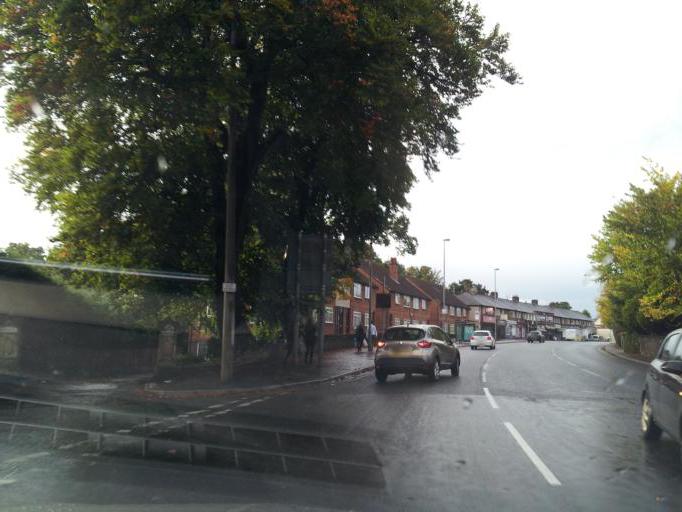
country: GB
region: England
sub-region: Manchester
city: Crumpsall
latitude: 53.5181
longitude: -2.2576
